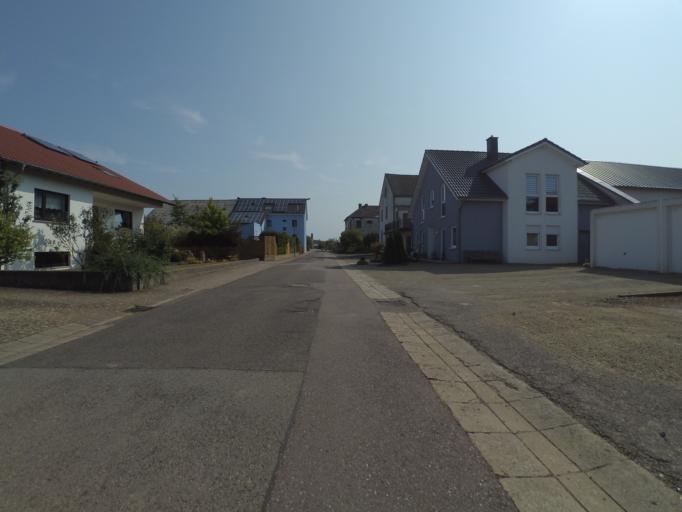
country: DE
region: Saarland
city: Orscholz
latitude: 49.4711
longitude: 6.4730
